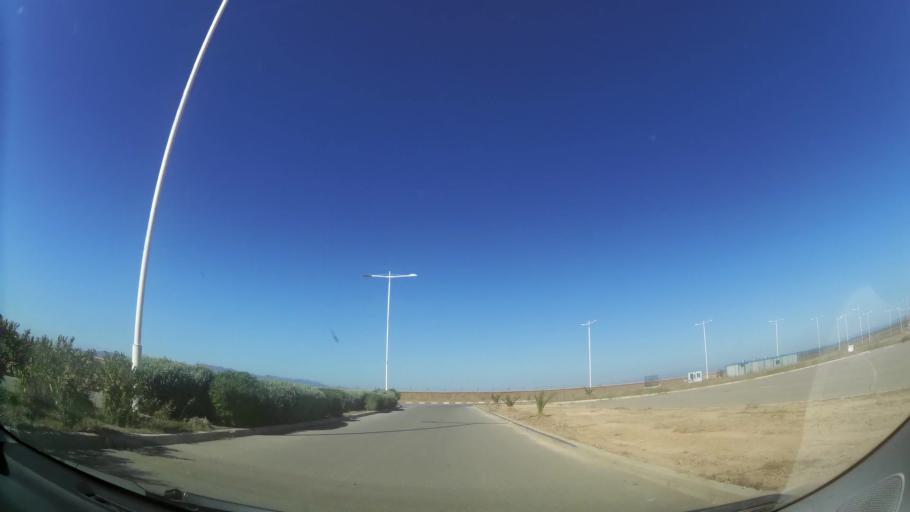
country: MA
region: Oriental
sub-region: Oujda-Angad
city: Oujda
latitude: 34.7764
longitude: -1.9345
